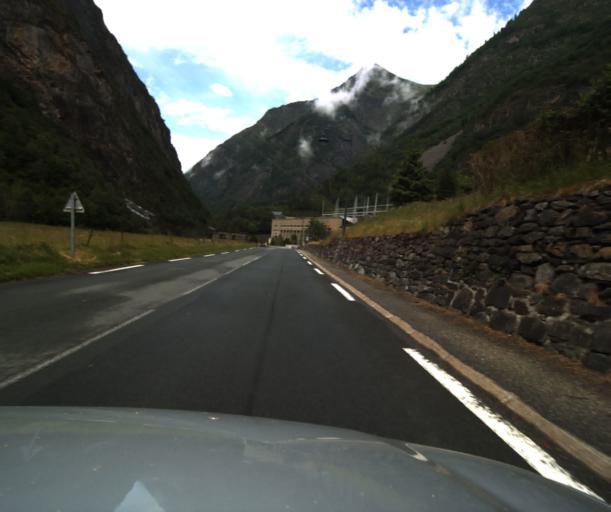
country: FR
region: Midi-Pyrenees
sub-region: Departement des Hautes-Pyrenees
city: Luz-Saint-Sauveur
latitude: 42.8193
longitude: 0.0102
